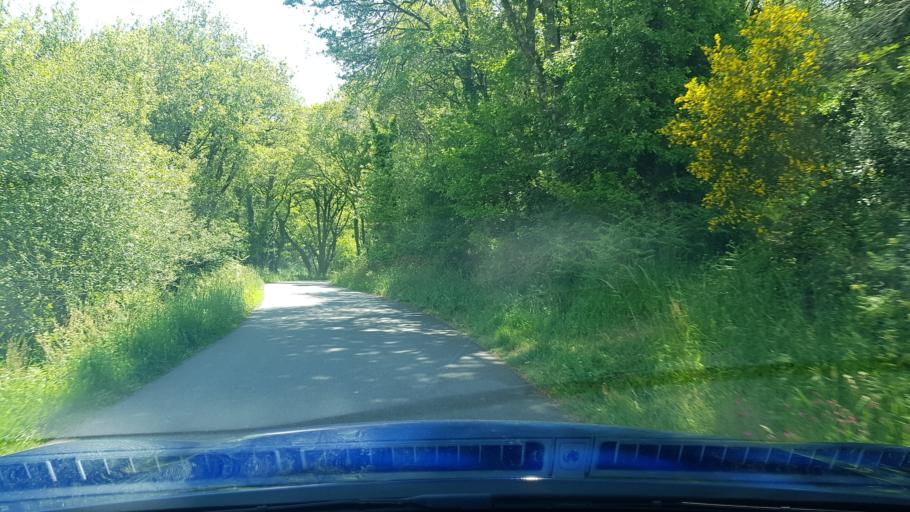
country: FR
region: Brittany
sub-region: Departement du Morbihan
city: Pont-Scorff
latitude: 47.8166
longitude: -3.4185
